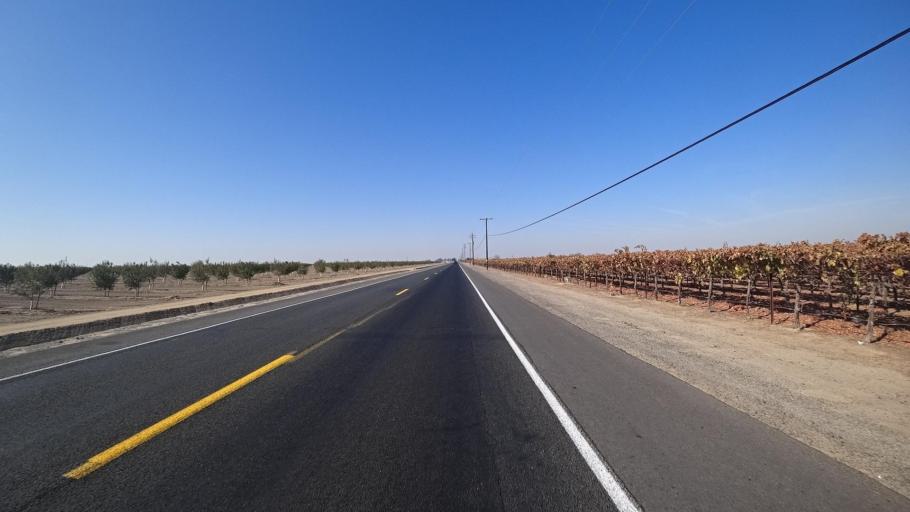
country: US
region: California
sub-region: Kern County
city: Delano
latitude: 35.7178
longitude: -119.2960
